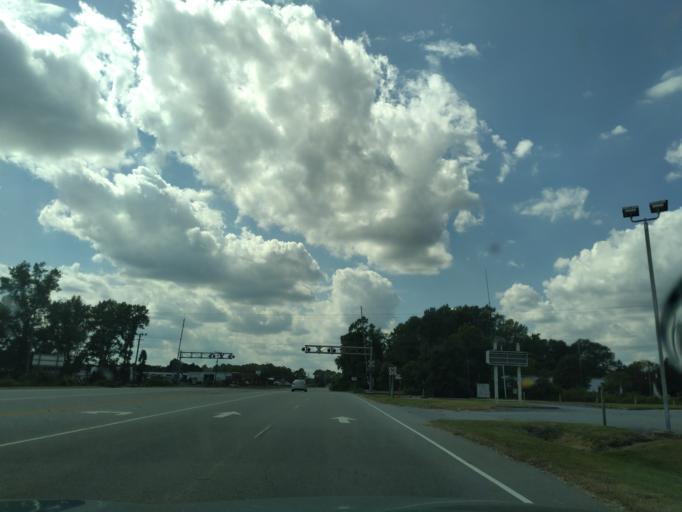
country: US
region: North Carolina
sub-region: Martin County
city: Williamston
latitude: 35.8432
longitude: -77.0577
